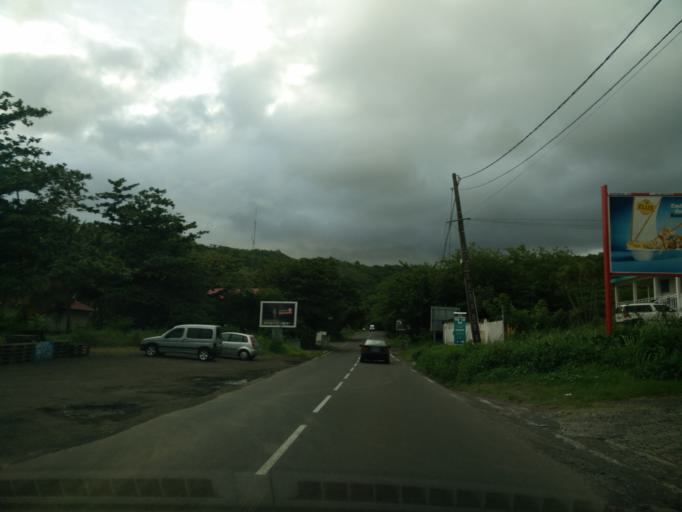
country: MQ
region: Martinique
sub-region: Martinique
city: Le Marin
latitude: 14.4710
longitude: -60.8575
